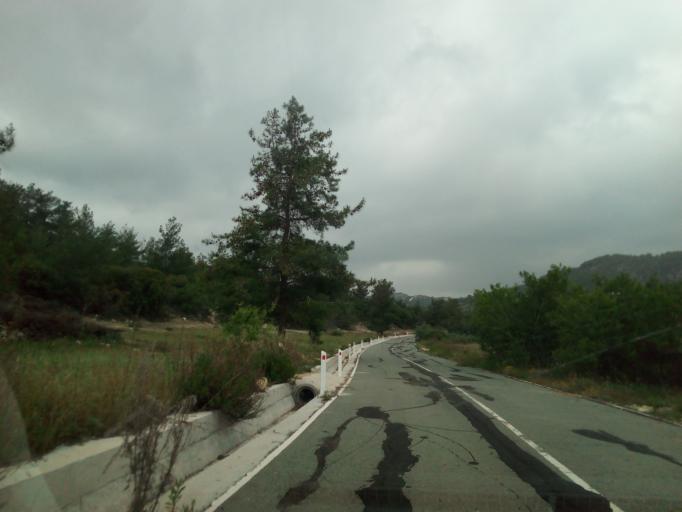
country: CY
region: Pafos
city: Mesogi
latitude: 34.8114
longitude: 32.6046
